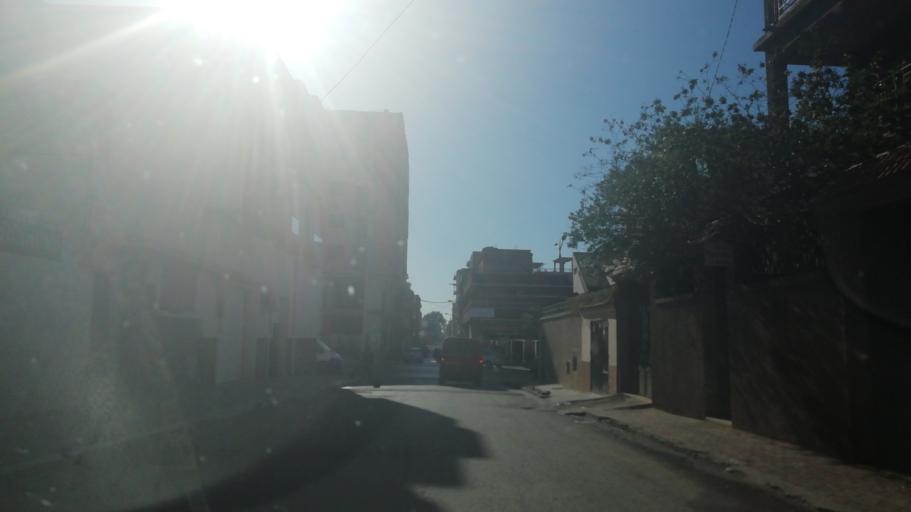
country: DZ
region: Oran
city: Oran
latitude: 35.6772
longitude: -0.6498
